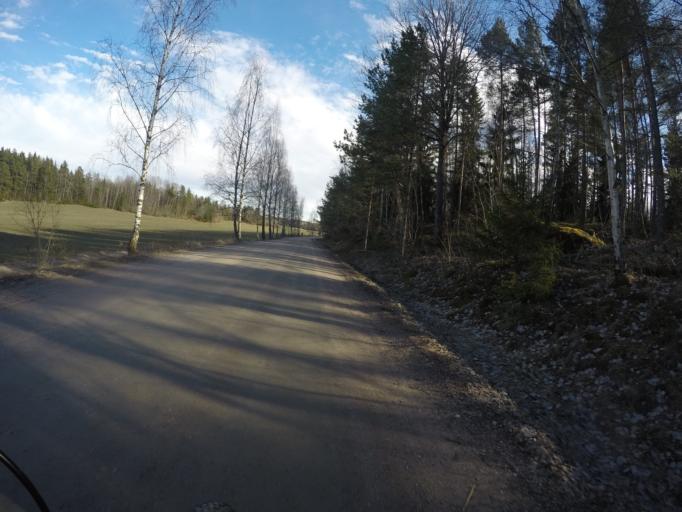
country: SE
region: Soedermanland
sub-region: Eskilstuna Kommun
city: Kvicksund
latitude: 59.4142
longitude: 16.2437
